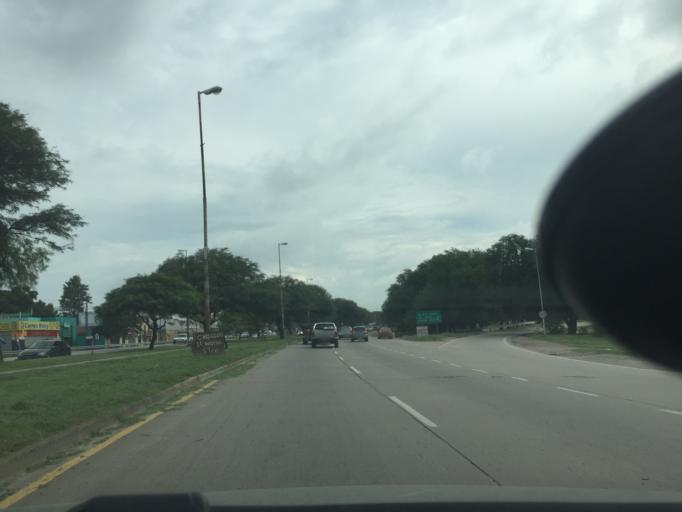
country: AR
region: Cordoba
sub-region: Departamento de Capital
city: Cordoba
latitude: -31.4644
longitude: -64.2216
